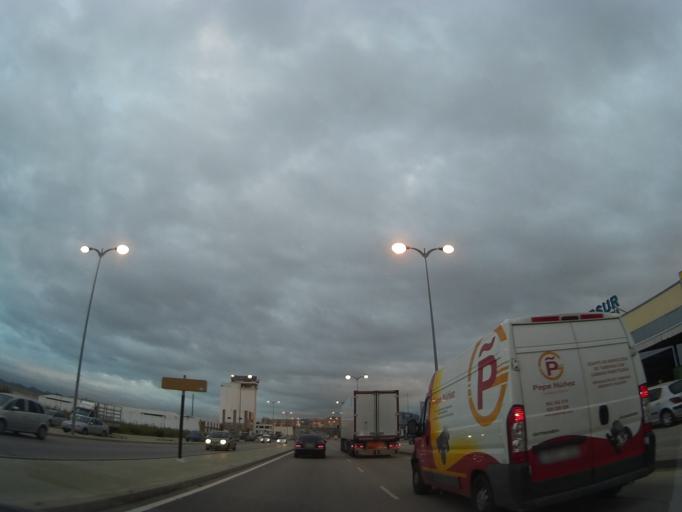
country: ES
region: Andalusia
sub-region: Provincia de Malaga
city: Alhaurin de la Torre
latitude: 36.6974
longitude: -4.4931
